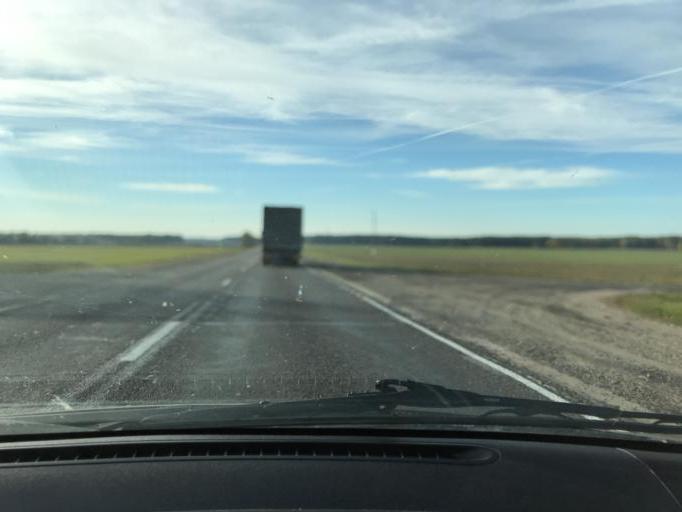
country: BY
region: Brest
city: Lahishyn
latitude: 52.1524
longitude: 25.8297
